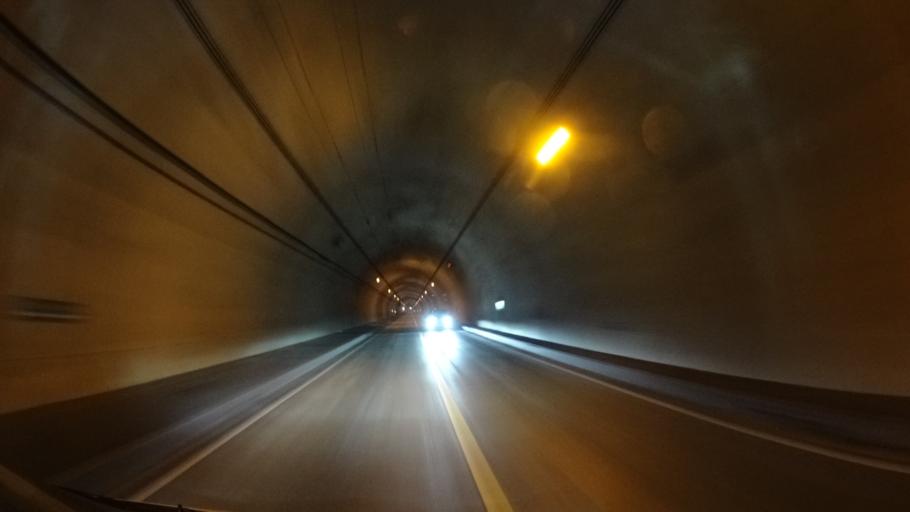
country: JP
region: Kyoto
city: Fukuchiyama
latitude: 35.4143
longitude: 135.0398
